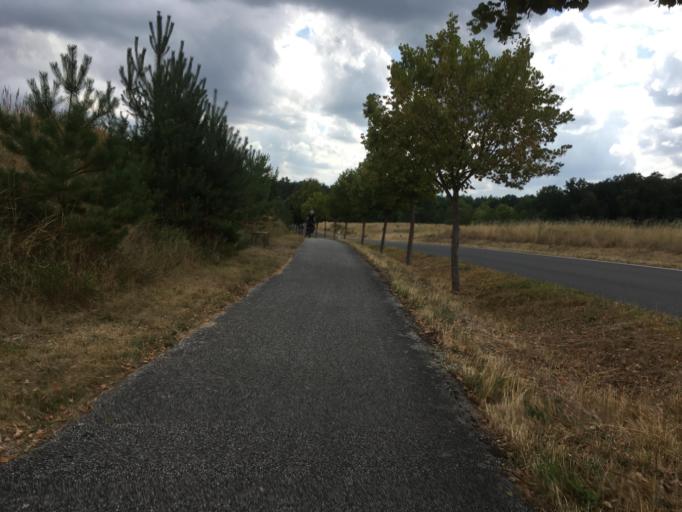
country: DE
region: Brandenburg
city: Lychen
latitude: 53.1683
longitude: 13.2381
